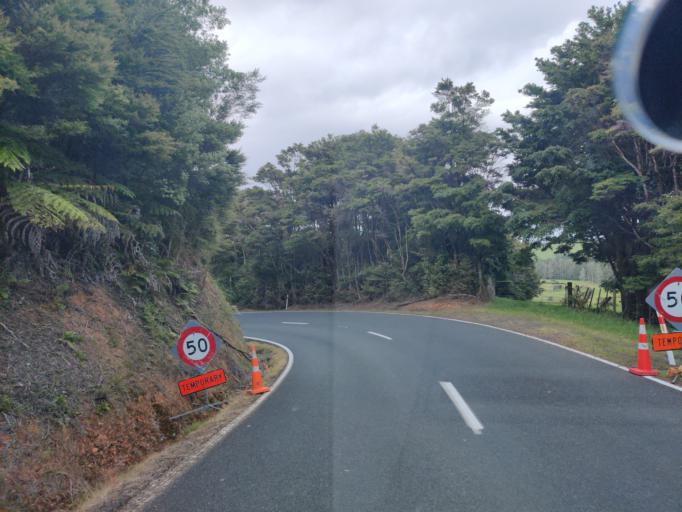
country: NZ
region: Northland
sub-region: Whangarei
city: Ngunguru
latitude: -35.5776
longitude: 174.4071
